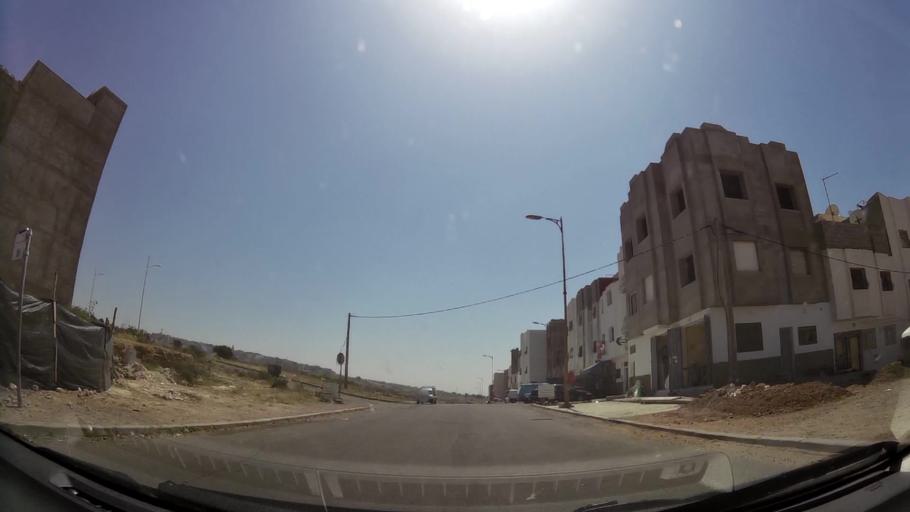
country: MA
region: Oued ed Dahab-Lagouira
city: Dakhla
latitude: 30.4425
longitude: -9.5562
